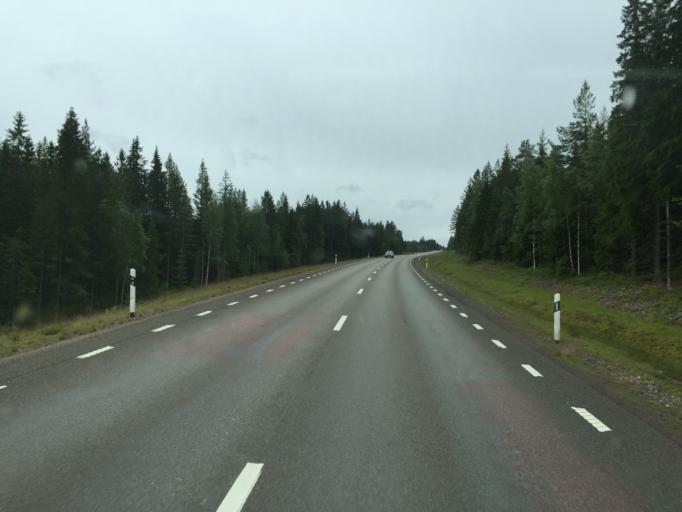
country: SE
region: Dalarna
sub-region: Malung-Saelens kommun
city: Malung
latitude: 60.5865
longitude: 13.5804
